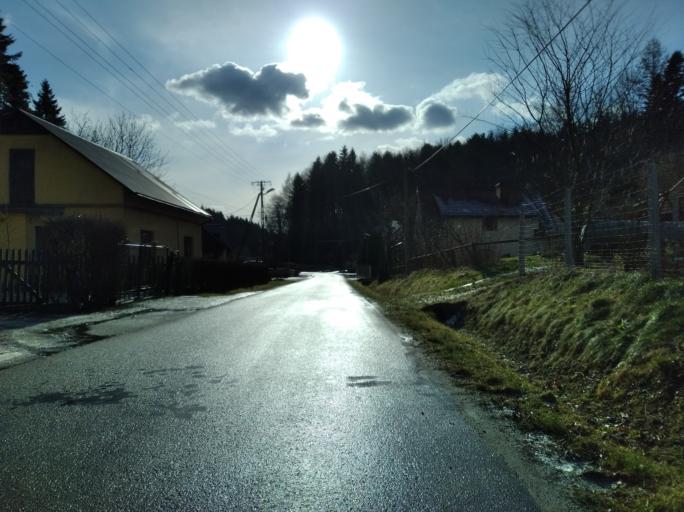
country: PL
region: Subcarpathian Voivodeship
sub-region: Powiat strzyzowski
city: Strzyzow
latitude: 49.8880
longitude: 21.7741
